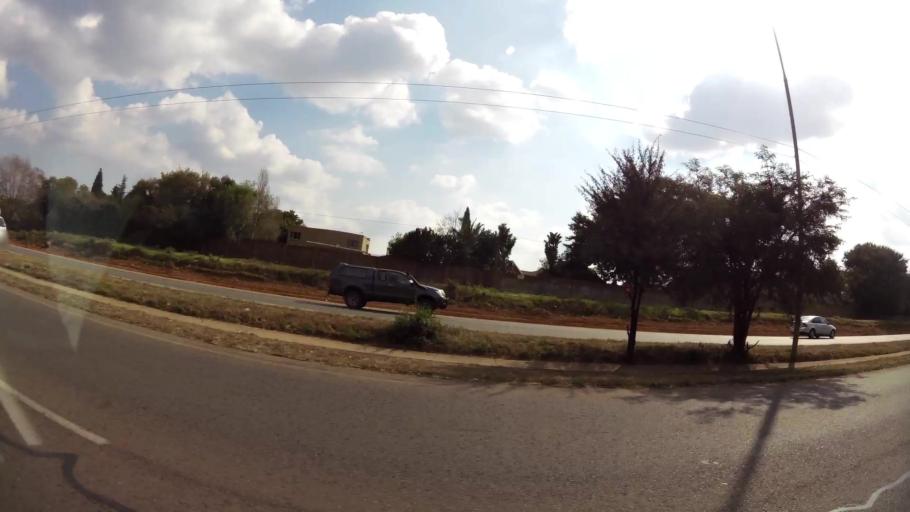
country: ZA
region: Gauteng
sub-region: City of Tshwane Metropolitan Municipality
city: Pretoria
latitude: -25.7929
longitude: 28.3251
